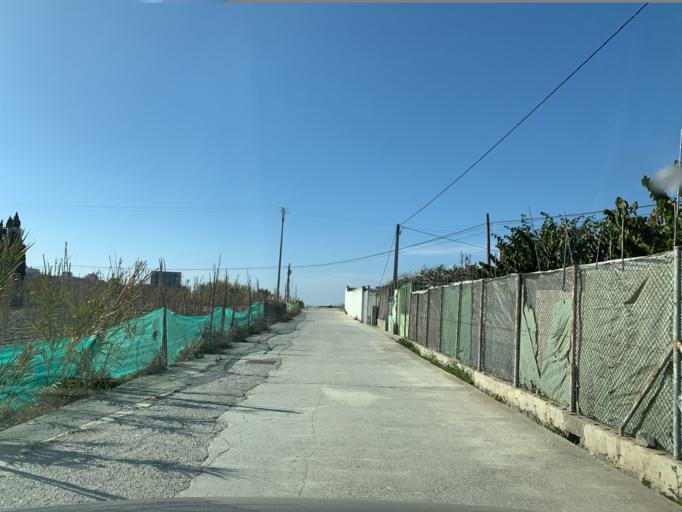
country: ES
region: Andalusia
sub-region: Provincia de Granada
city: Salobrena
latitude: 36.7252
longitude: -3.5581
